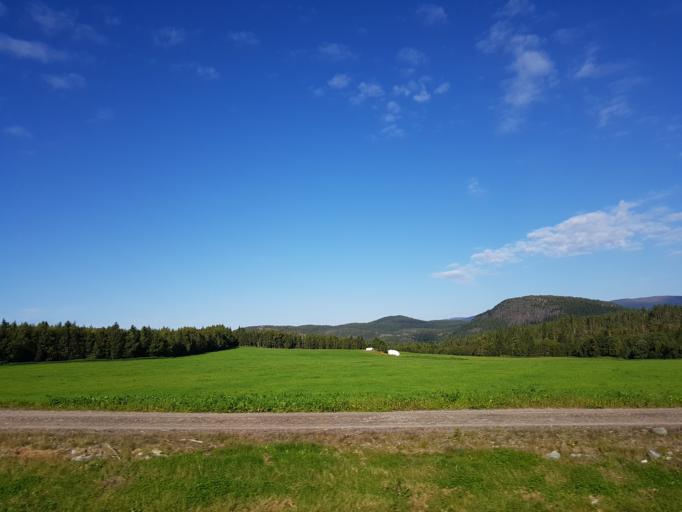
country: NO
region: Sor-Trondelag
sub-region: Rissa
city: Rissa
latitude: 63.5913
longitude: 10.1949
